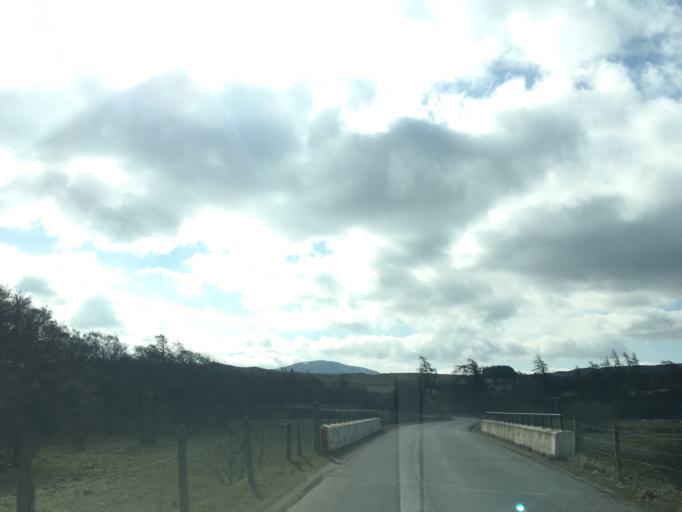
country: GB
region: Scotland
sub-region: Highland
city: Kingussie
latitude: 57.0740
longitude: -4.0487
